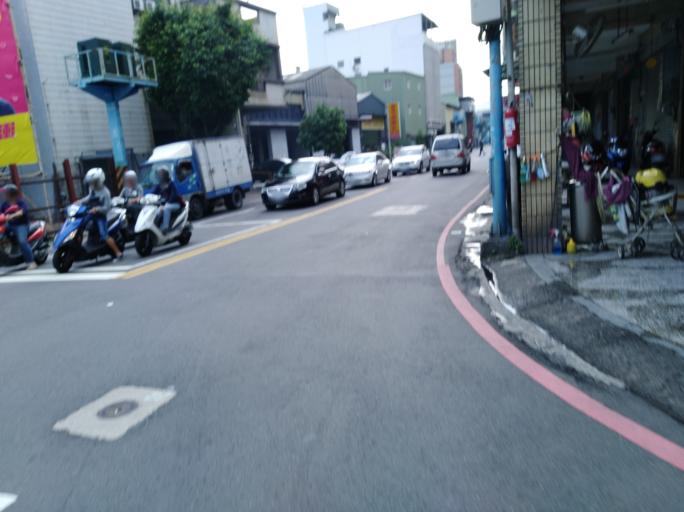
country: TW
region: Taipei
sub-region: Taipei
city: Banqiao
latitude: 25.0284
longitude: 121.4348
